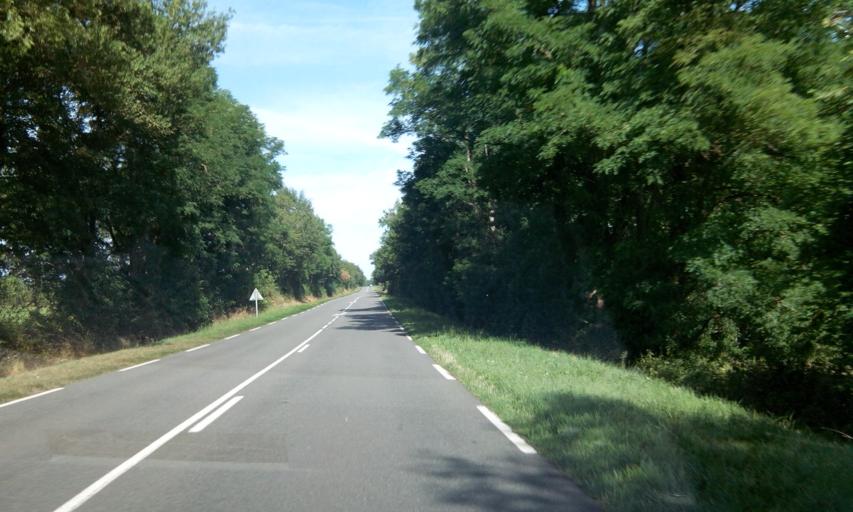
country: FR
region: Poitou-Charentes
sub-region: Departement de la Charente
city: Chabanais
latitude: 45.9468
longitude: 0.7226
